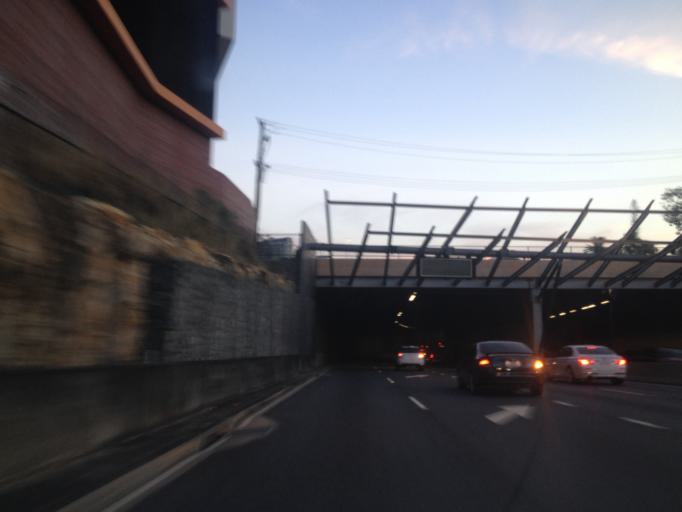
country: AU
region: Queensland
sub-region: Brisbane
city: Fortitude Valley
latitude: -27.4475
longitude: 153.0313
